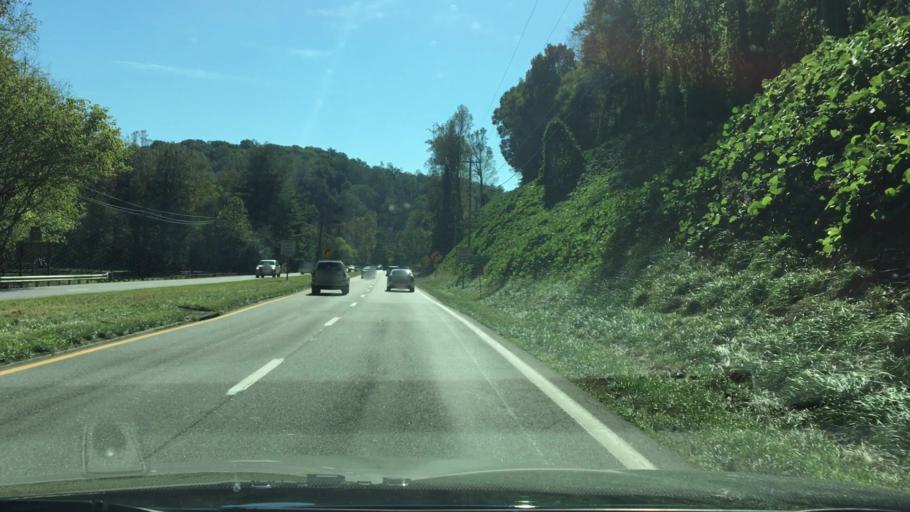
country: US
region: Virginia
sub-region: Roanoke County
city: Narrows
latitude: 37.1240
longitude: -79.9584
